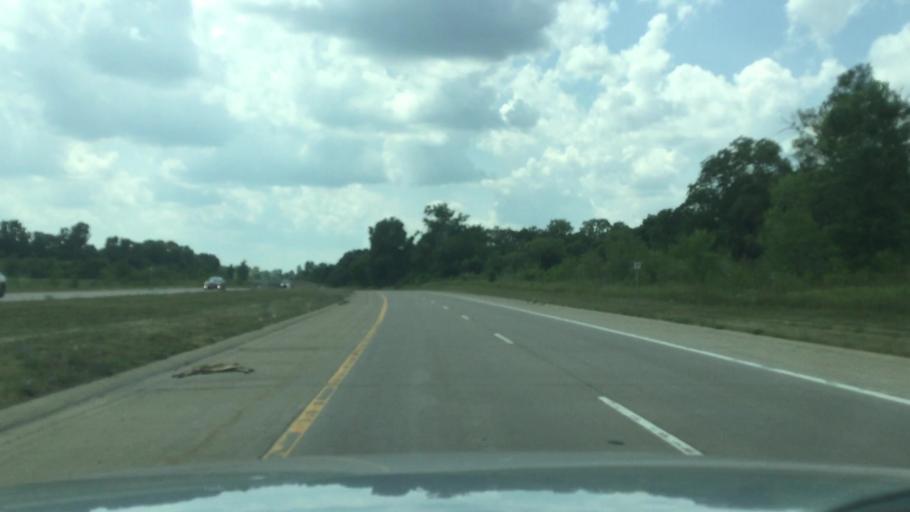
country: US
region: Michigan
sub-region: Wayne County
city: Belleville
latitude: 42.2566
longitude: -83.5356
